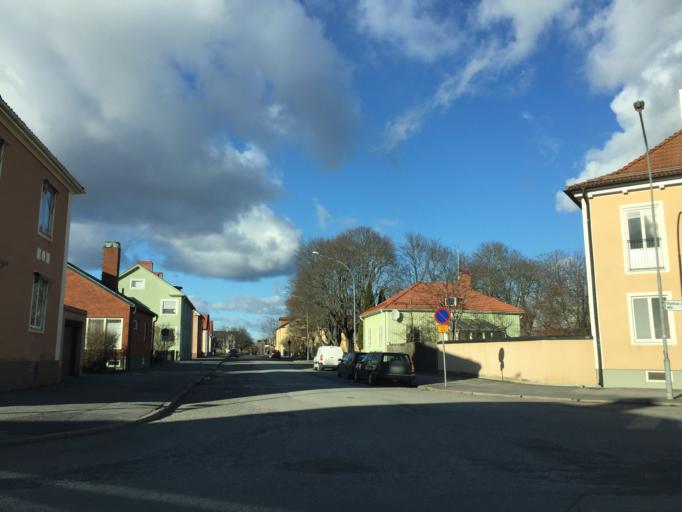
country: SE
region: OErebro
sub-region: Orebro Kommun
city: Orebro
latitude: 59.2822
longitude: 15.2100
